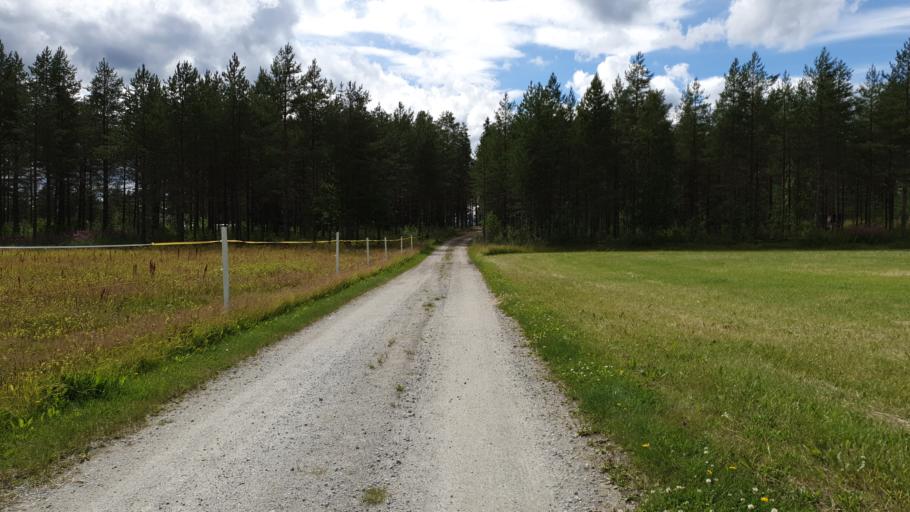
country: FI
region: Kainuu
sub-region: Kehys-Kainuu
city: Kuhmo
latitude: 64.3827
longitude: 29.8090
